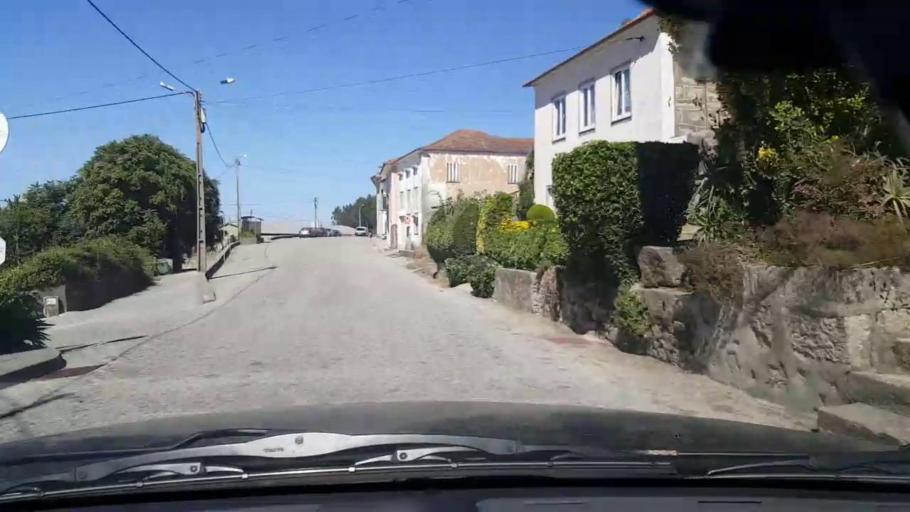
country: PT
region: Porto
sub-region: Maia
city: Gemunde
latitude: 41.3274
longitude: -8.6432
